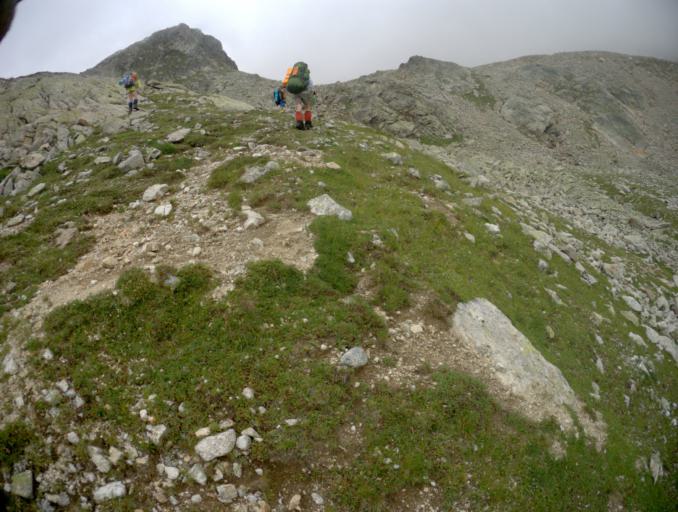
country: RU
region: Karachayevo-Cherkesiya
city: Uchkulan
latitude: 43.2831
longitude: 42.1011
